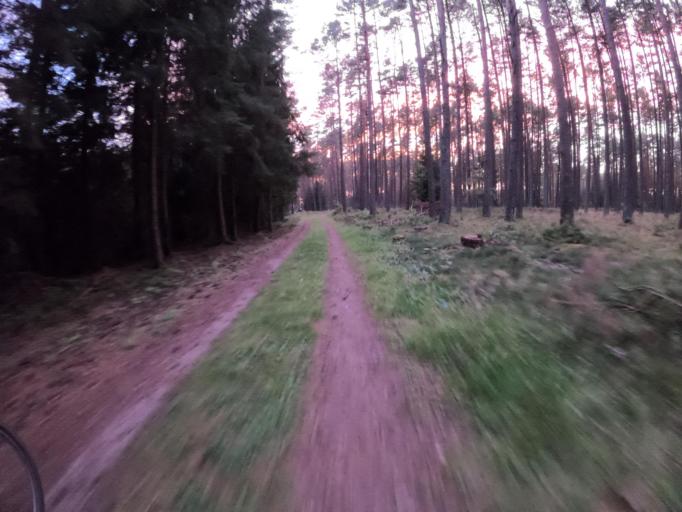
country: PL
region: West Pomeranian Voivodeship
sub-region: Powiat koszalinski
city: Sianow
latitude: 54.0700
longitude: 16.3797
